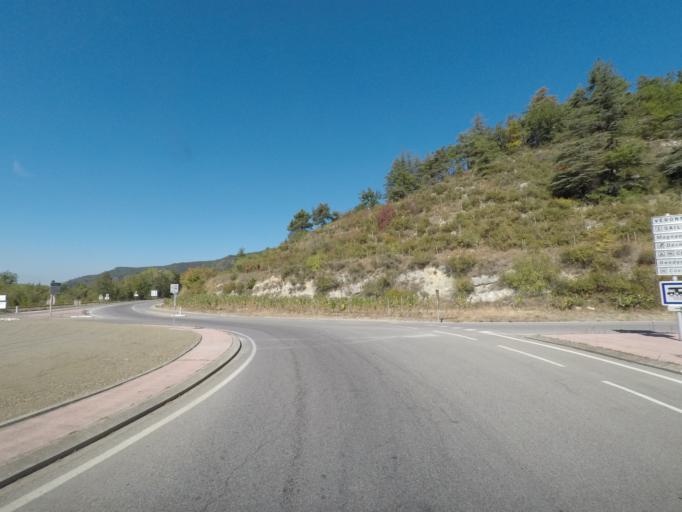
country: FR
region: Rhone-Alpes
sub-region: Departement de la Drome
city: Aouste-sur-Sye
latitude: 44.6938
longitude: 5.1706
